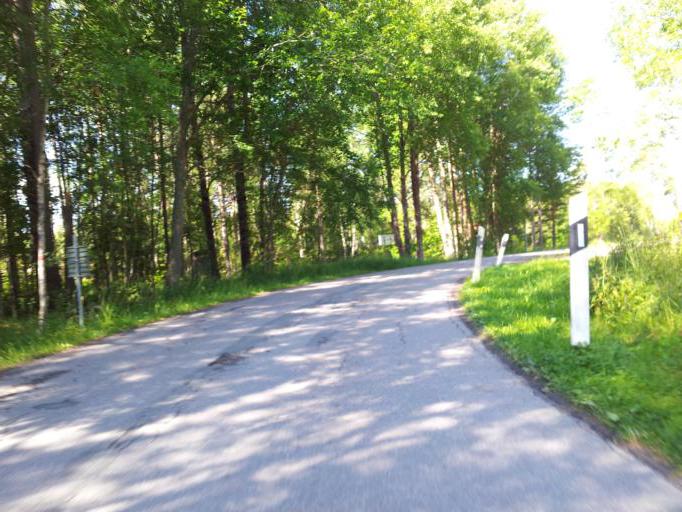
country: SE
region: Uppsala
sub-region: Uppsala Kommun
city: Saevja
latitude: 59.8745
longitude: 17.7450
